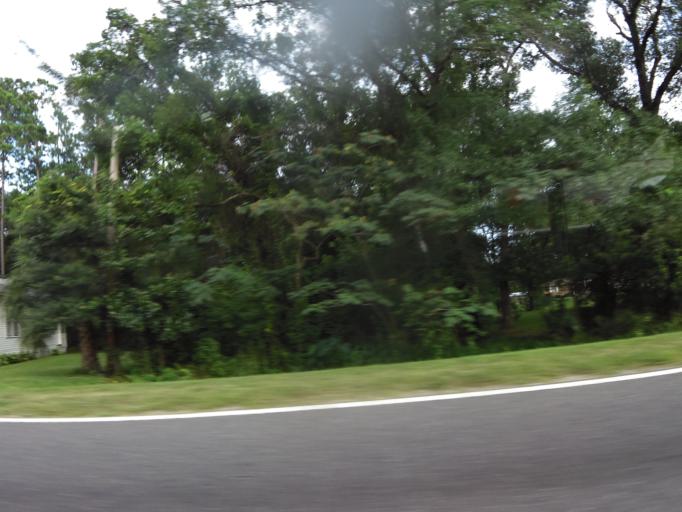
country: US
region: Florida
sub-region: Duval County
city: Jacksonville
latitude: 30.3637
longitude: -81.7428
